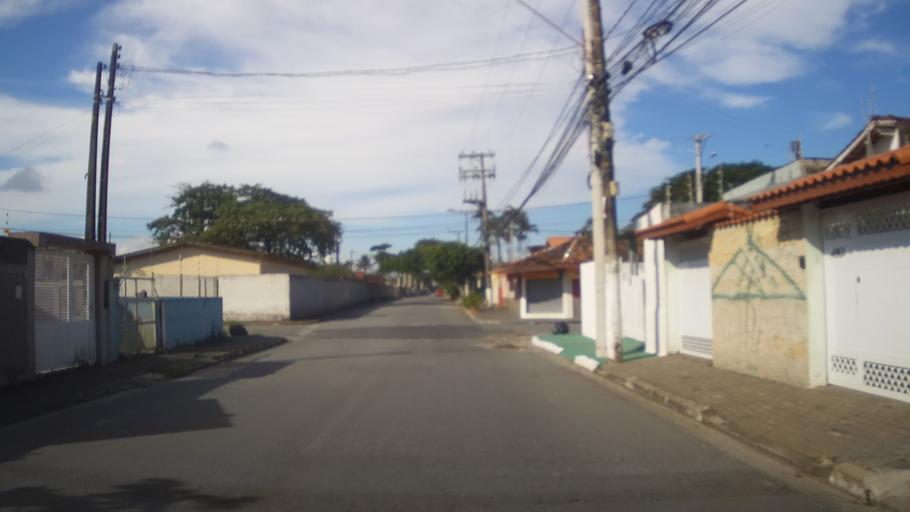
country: BR
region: Sao Paulo
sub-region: Itanhaem
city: Itanhaem
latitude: -24.1648
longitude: -46.7524
